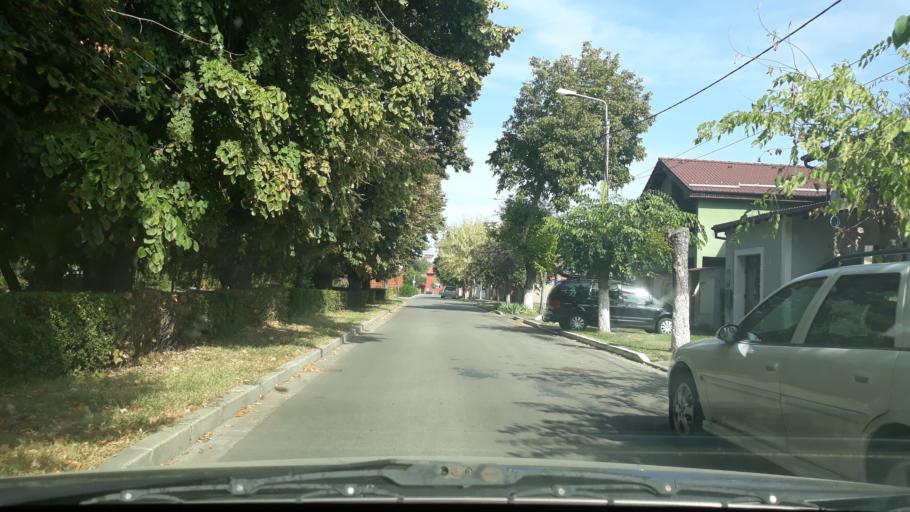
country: RO
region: Bihor
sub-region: Comuna Biharea
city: Oradea
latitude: 47.0444
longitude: 21.9372
